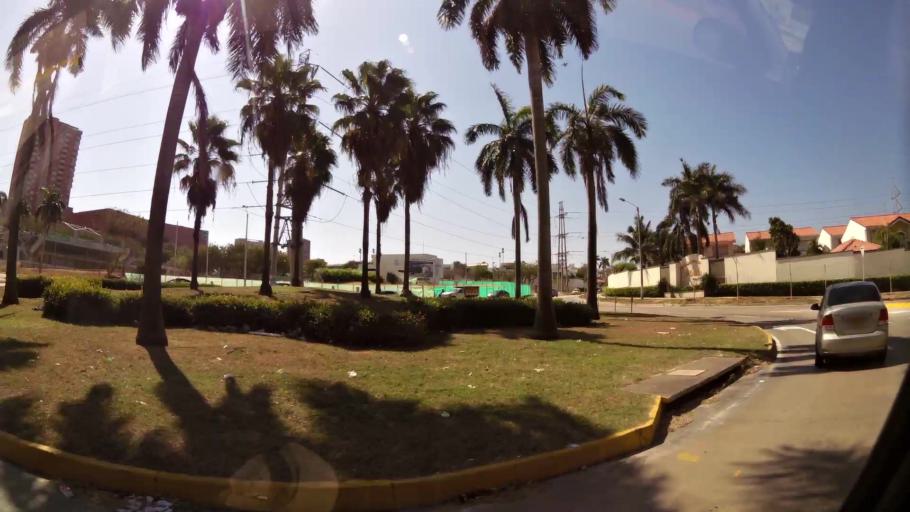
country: CO
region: Atlantico
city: Barranquilla
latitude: 11.0153
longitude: -74.8307
